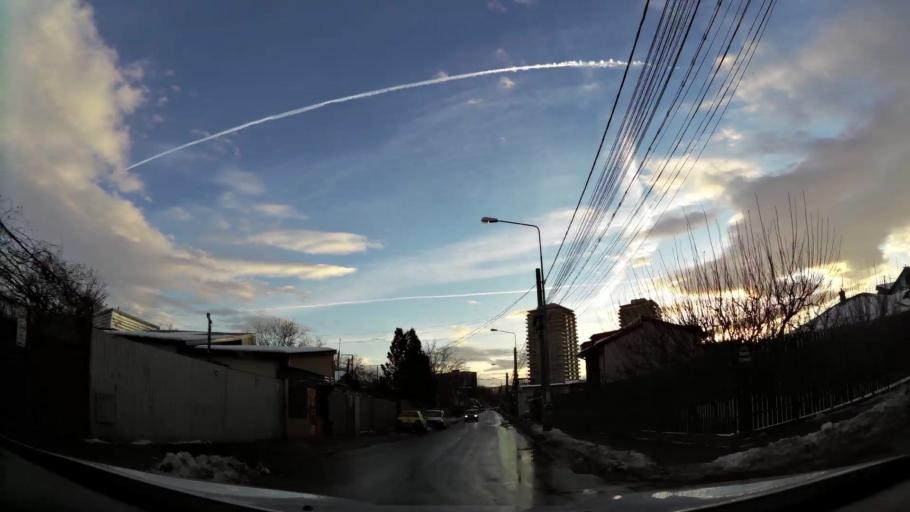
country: RO
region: Ilfov
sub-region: Comuna Popesti-Leordeni
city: Popesti-Leordeni
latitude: 44.3733
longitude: 26.1434
